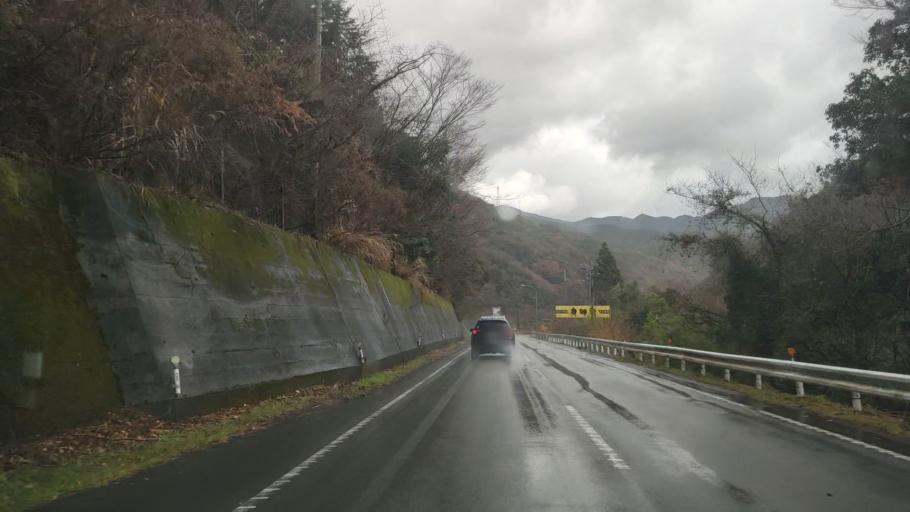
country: JP
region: Tokushima
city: Kamojimacho-jogejima
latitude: 34.1648
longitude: 134.3375
